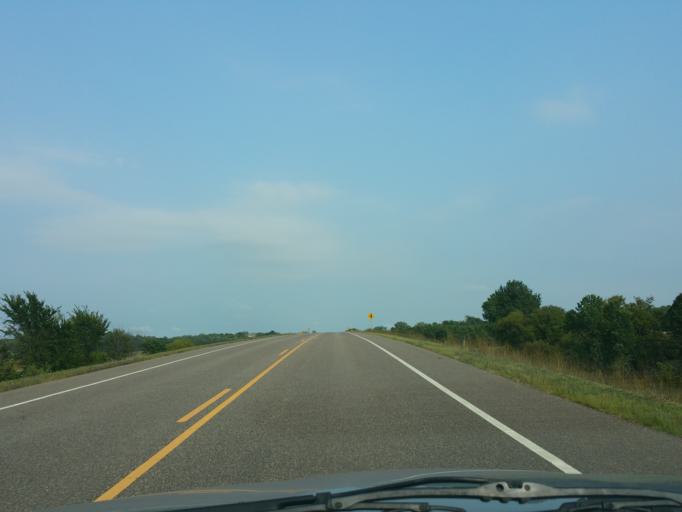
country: US
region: Minnesota
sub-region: Washington County
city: Lake Saint Croix Beach
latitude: 44.9311
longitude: -92.6882
